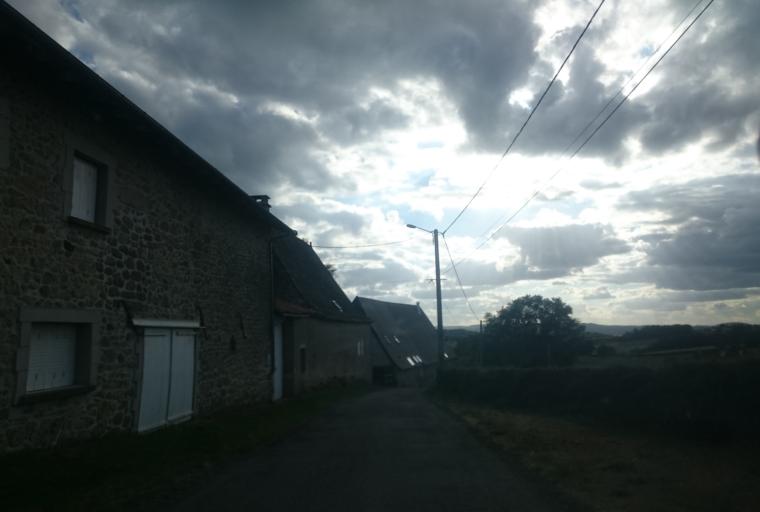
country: FR
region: Auvergne
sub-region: Departement du Cantal
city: Saint-Mamet-la-Salvetat
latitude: 44.8550
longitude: 2.2703
